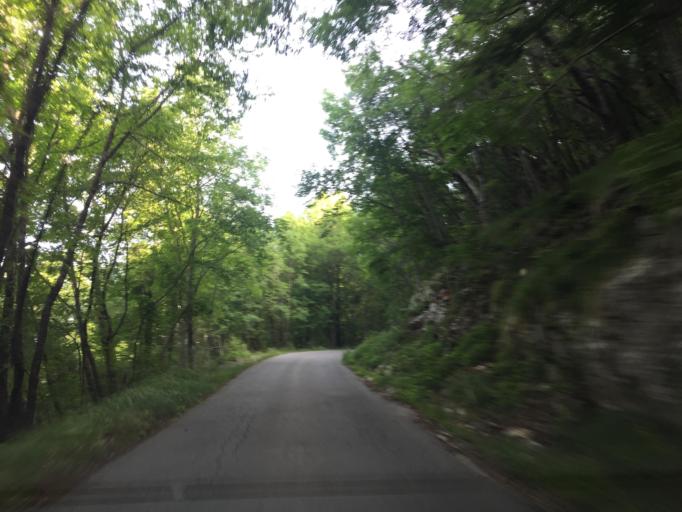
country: HR
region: Primorsko-Goranska
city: Klana
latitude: 45.4827
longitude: 14.4168
